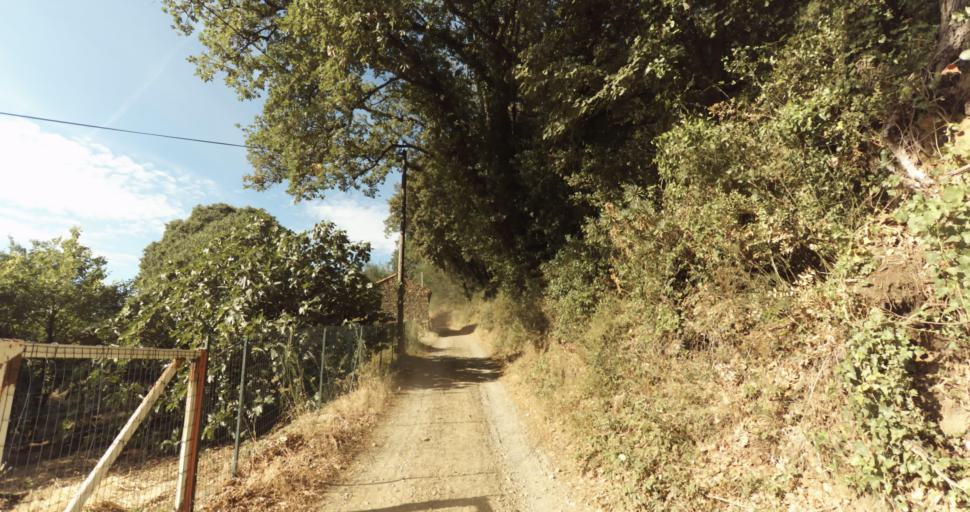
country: FR
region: Provence-Alpes-Cote d'Azur
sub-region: Departement du Var
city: Gassin
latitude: 43.2293
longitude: 6.5803
